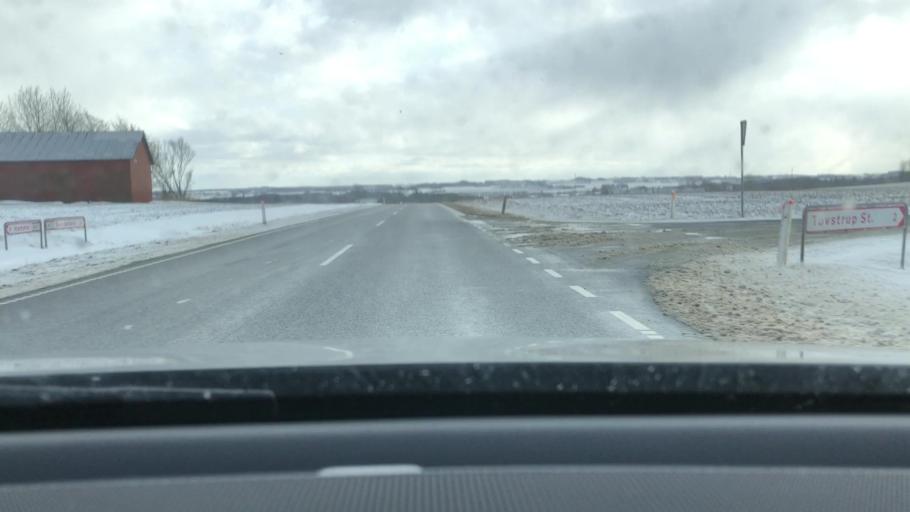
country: DK
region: Central Jutland
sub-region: Skanderborg Kommune
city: Galten
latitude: 56.1842
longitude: 9.8488
